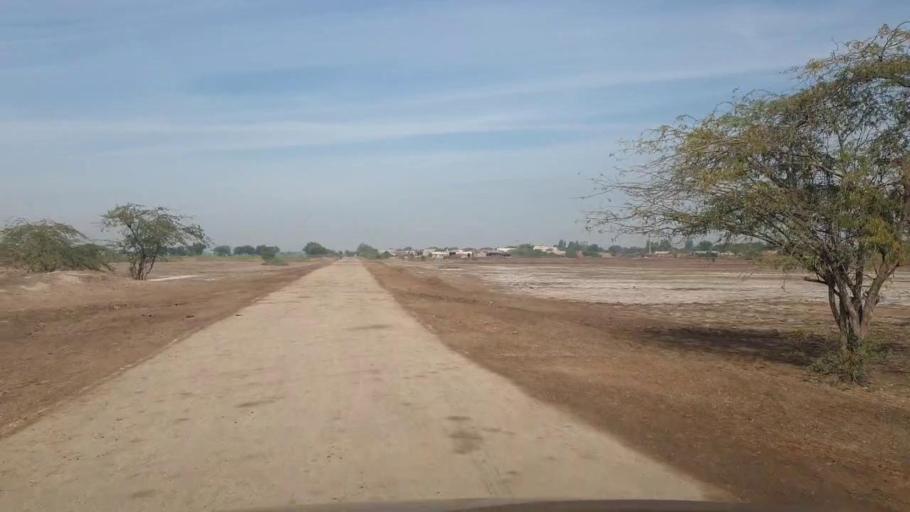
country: PK
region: Sindh
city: Umarkot
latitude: 25.3539
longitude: 69.6786
